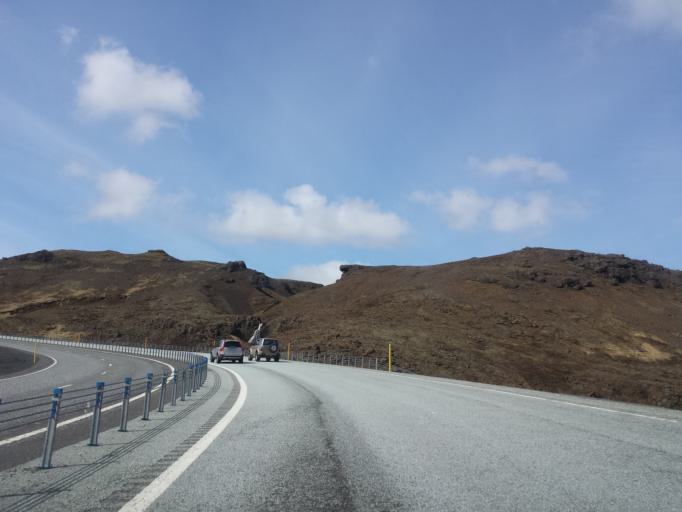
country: IS
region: South
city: Hveragerdi
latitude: 64.0162
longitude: -21.2294
